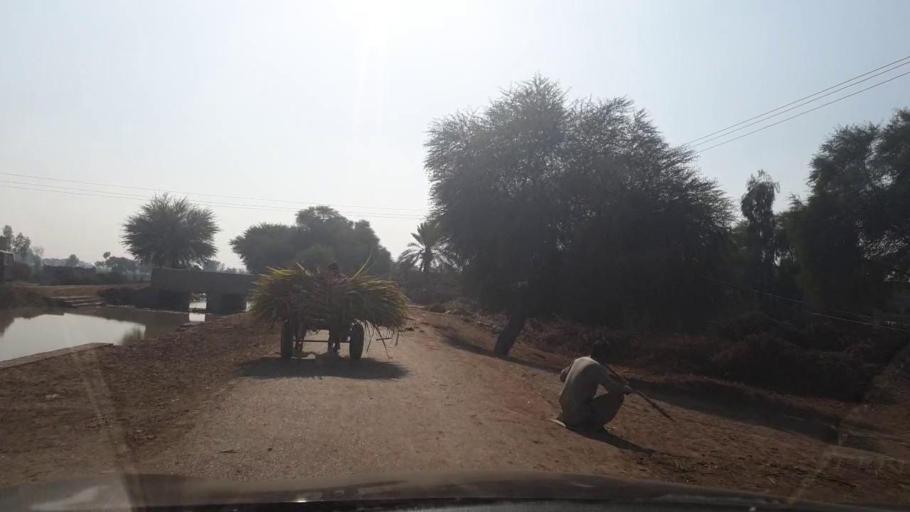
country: PK
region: Sindh
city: Ubauro
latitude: 28.1358
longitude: 69.6485
